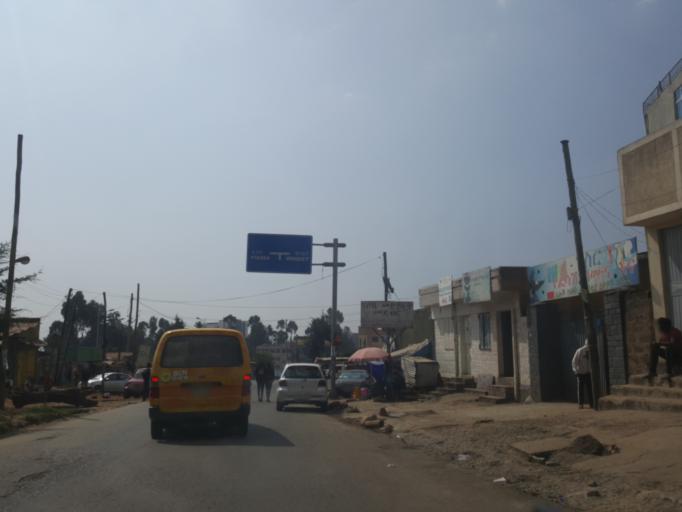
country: ET
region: Adis Abeba
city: Addis Ababa
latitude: 9.0538
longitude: 38.7201
